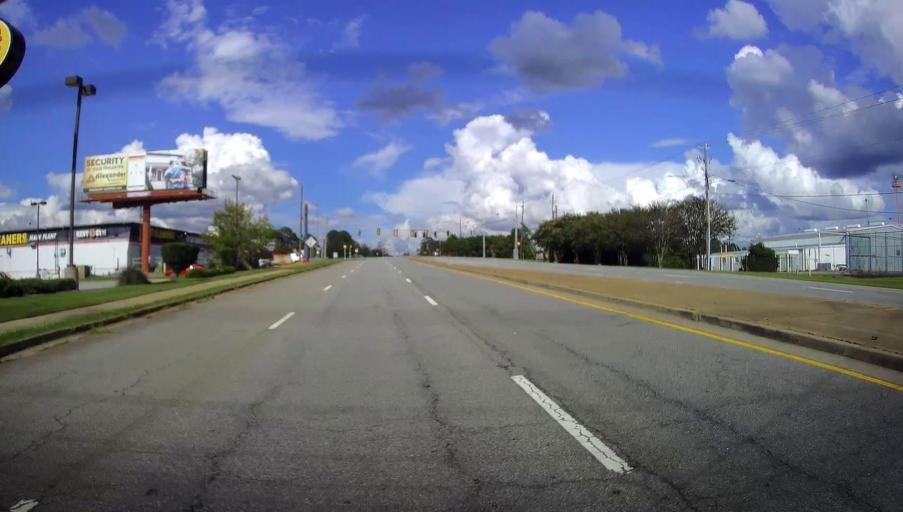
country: US
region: Georgia
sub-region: Muscogee County
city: Columbus
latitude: 32.5208
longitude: -84.9479
